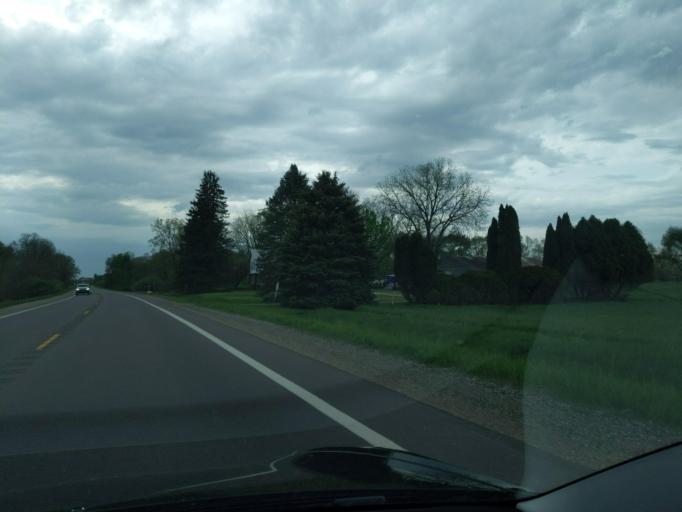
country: US
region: Michigan
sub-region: Ingham County
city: Stockbridge
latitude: 42.4073
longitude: -84.1236
